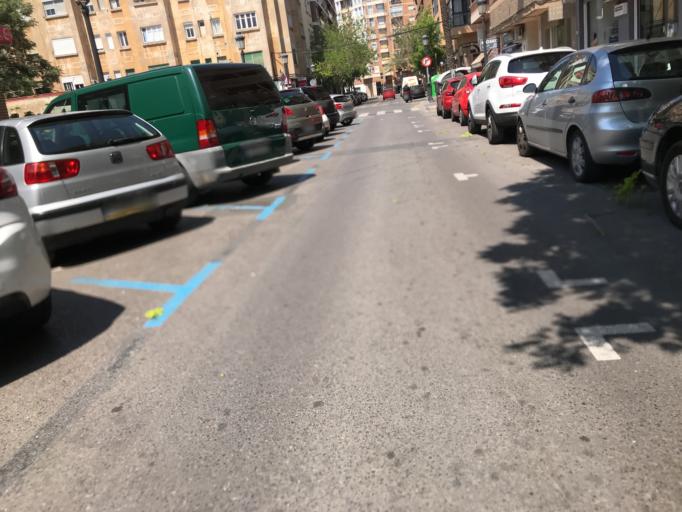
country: ES
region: Valencia
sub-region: Provincia de Valencia
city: Valencia
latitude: 39.4700
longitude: -0.3531
